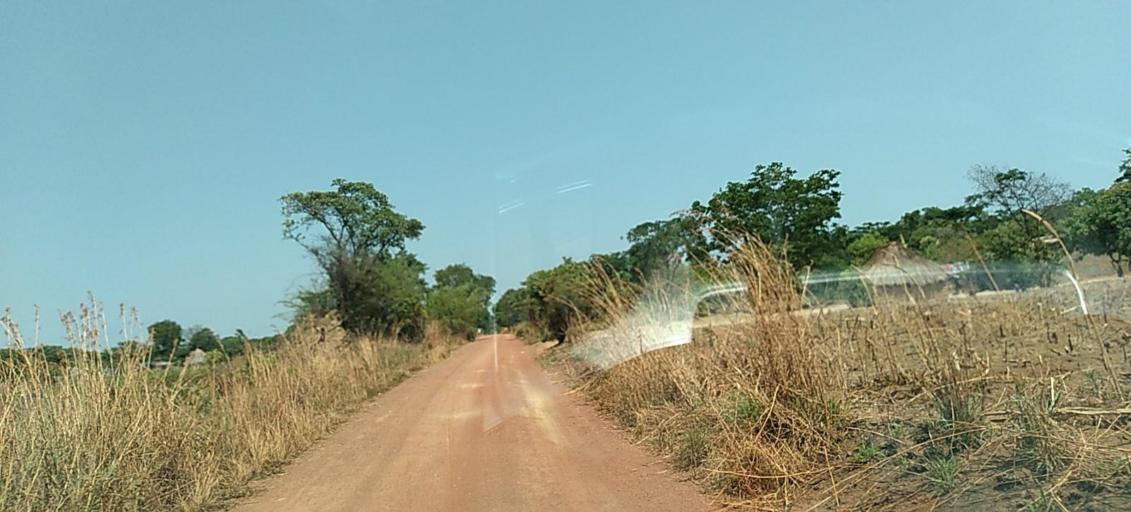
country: ZM
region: Copperbelt
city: Chingola
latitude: -12.5426
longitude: 27.7410
